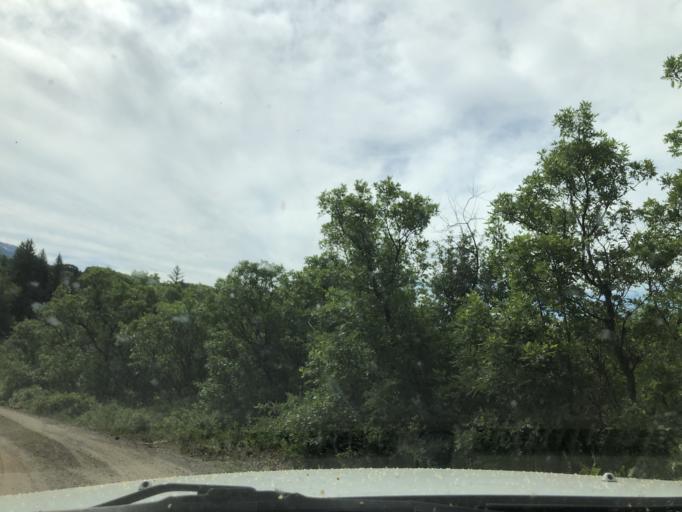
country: US
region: Colorado
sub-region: Delta County
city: Paonia
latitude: 39.0273
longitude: -107.3447
